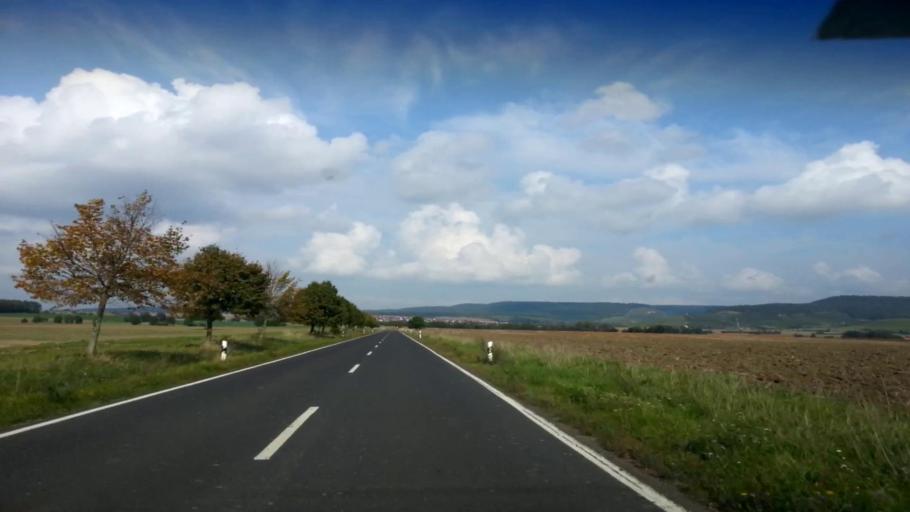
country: DE
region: Bavaria
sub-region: Regierungsbezirk Unterfranken
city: Oberschwarzach
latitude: 49.8410
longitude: 10.4073
